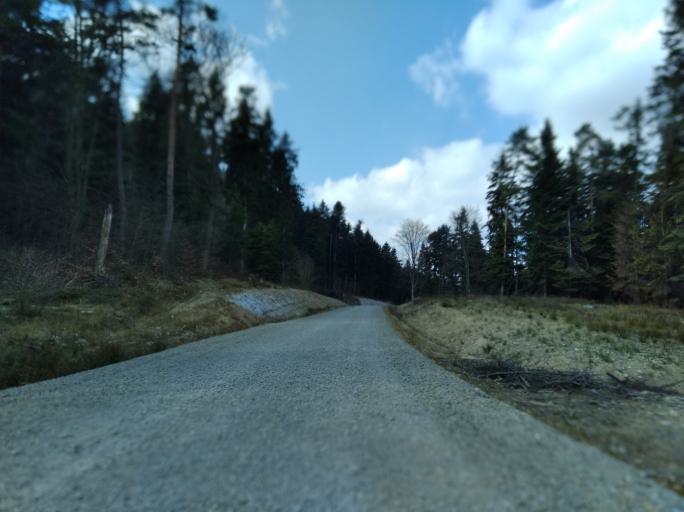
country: PL
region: Subcarpathian Voivodeship
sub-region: Powiat strzyzowski
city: Strzyzow
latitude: 49.8186
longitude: 21.8091
